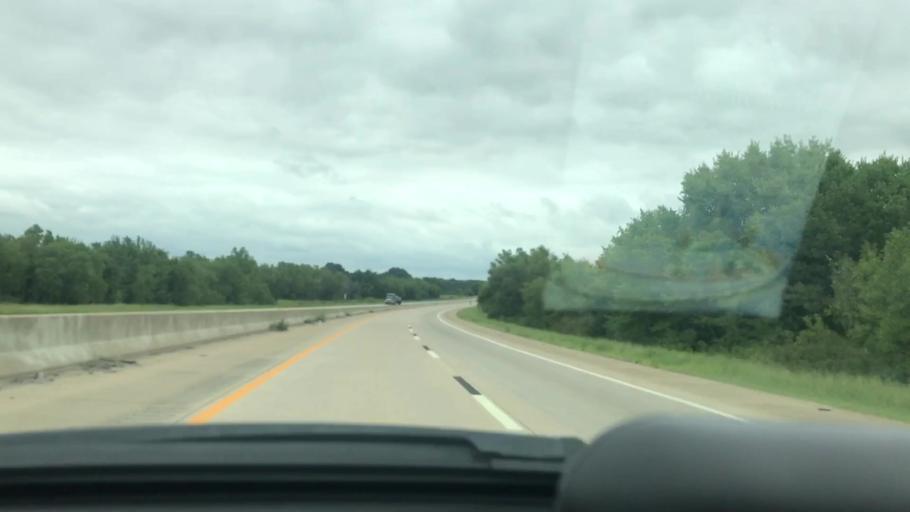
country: US
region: Oklahoma
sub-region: McIntosh County
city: Eufaula
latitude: 35.1907
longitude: -95.6382
